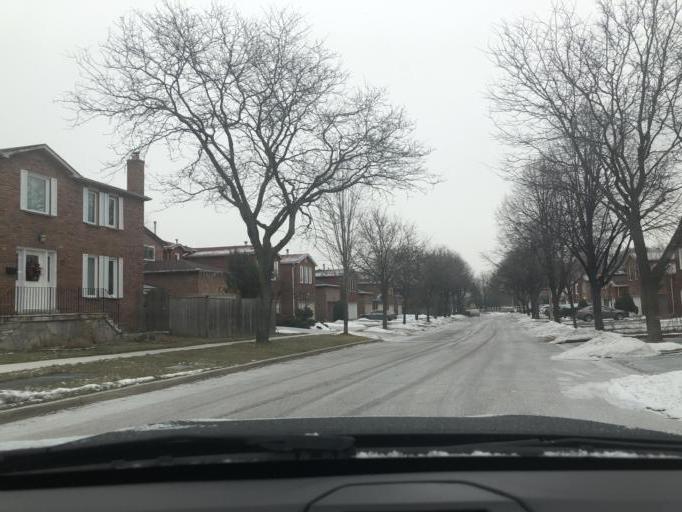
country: CA
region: Ontario
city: Scarborough
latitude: 43.7819
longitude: -79.2683
